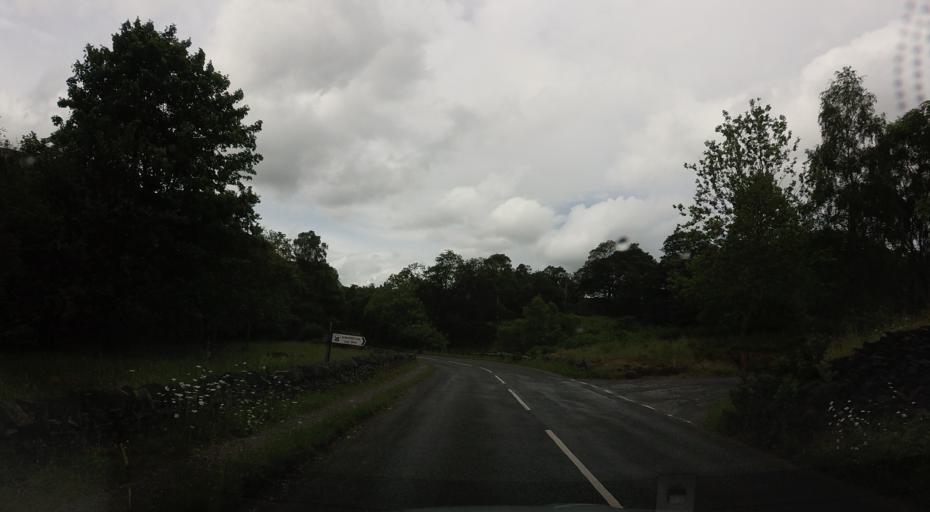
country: GB
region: England
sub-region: Cumbria
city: Keswick
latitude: 54.5415
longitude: -3.1563
